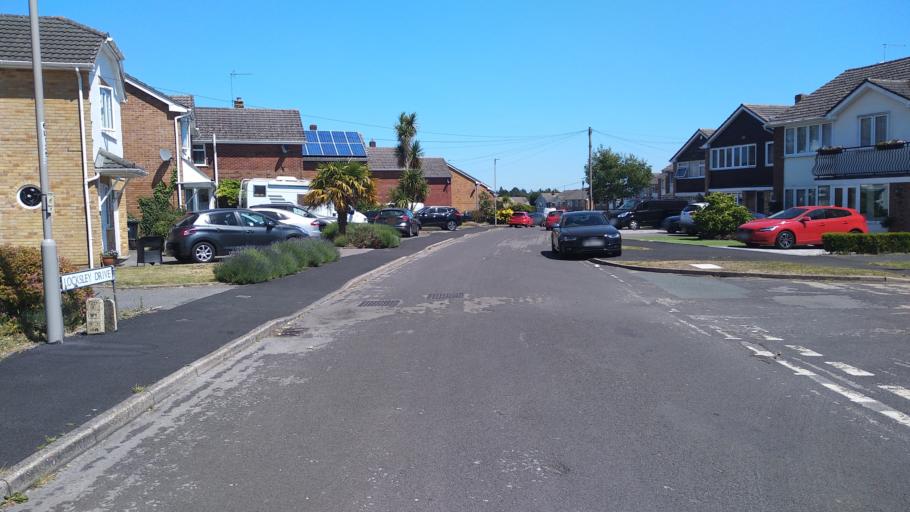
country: GB
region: England
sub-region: Dorset
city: Ferndown
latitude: 50.7925
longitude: -1.8984
